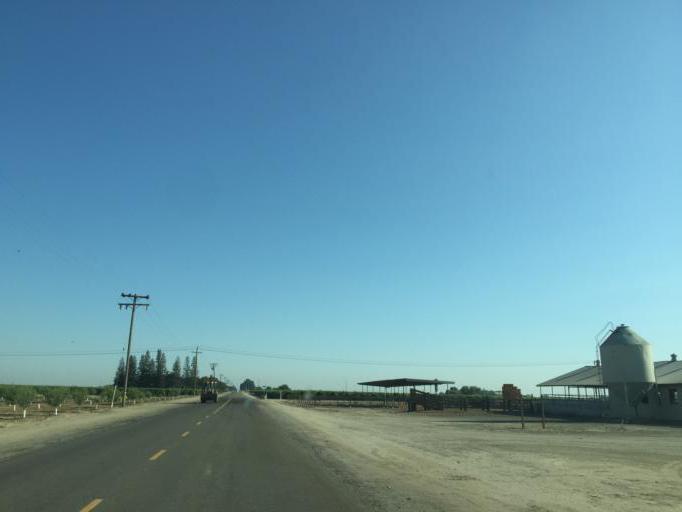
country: US
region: California
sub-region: Fresno County
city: Kingsburg
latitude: 36.4758
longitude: -119.5284
